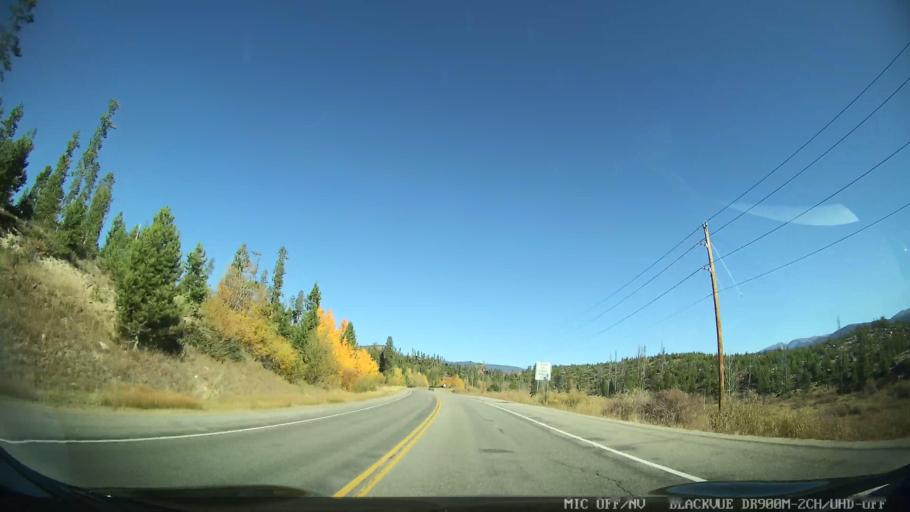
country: US
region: Colorado
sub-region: Grand County
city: Granby
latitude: 40.2090
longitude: -105.8603
